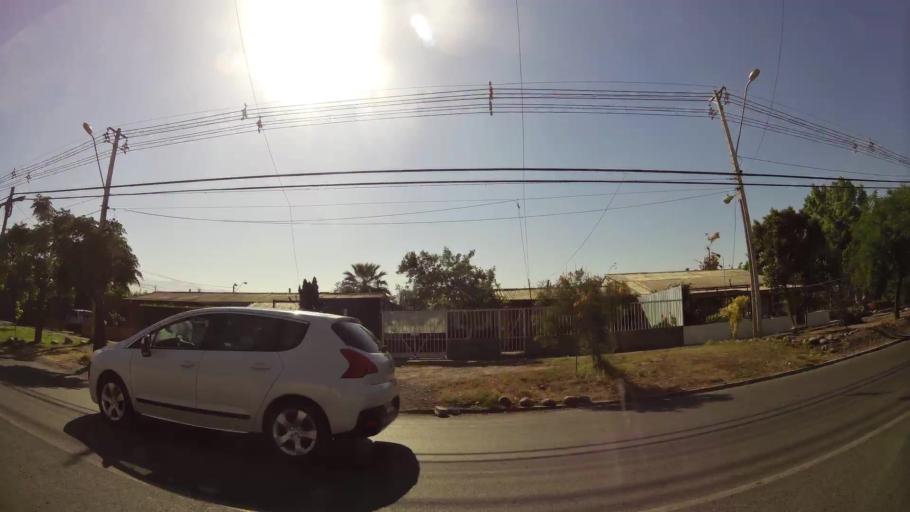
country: CL
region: Santiago Metropolitan
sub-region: Provincia de Maipo
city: San Bernardo
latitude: -33.5721
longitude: -70.7005
